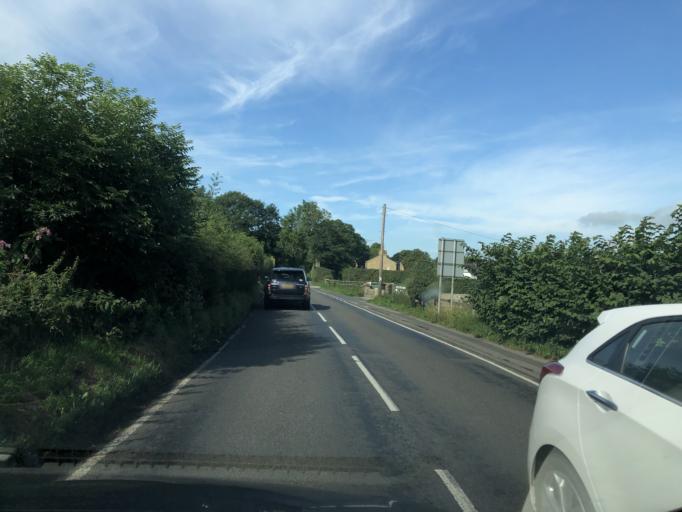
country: GB
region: England
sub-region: City and Borough of Leeds
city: Pool
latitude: 53.8995
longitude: -1.6137
